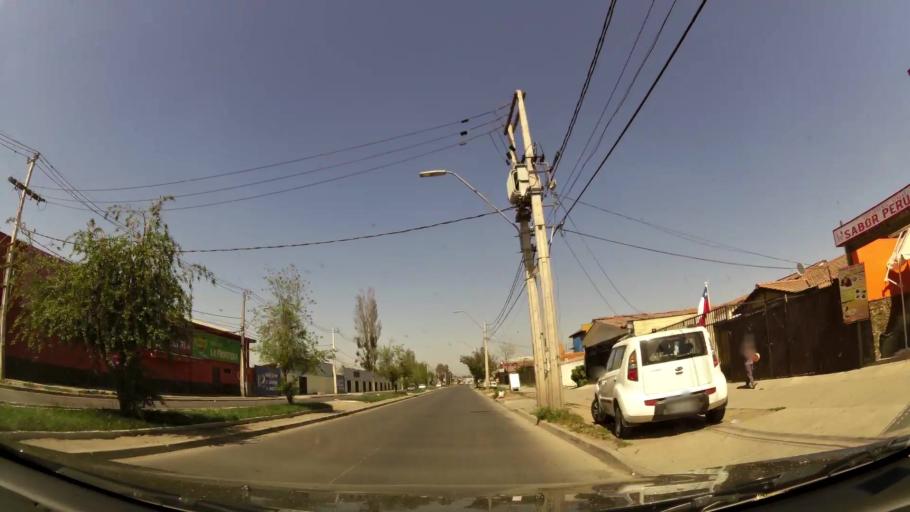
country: CL
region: Santiago Metropolitan
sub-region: Provincia de Santiago
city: Lo Prado
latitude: -33.4010
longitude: -70.7464
